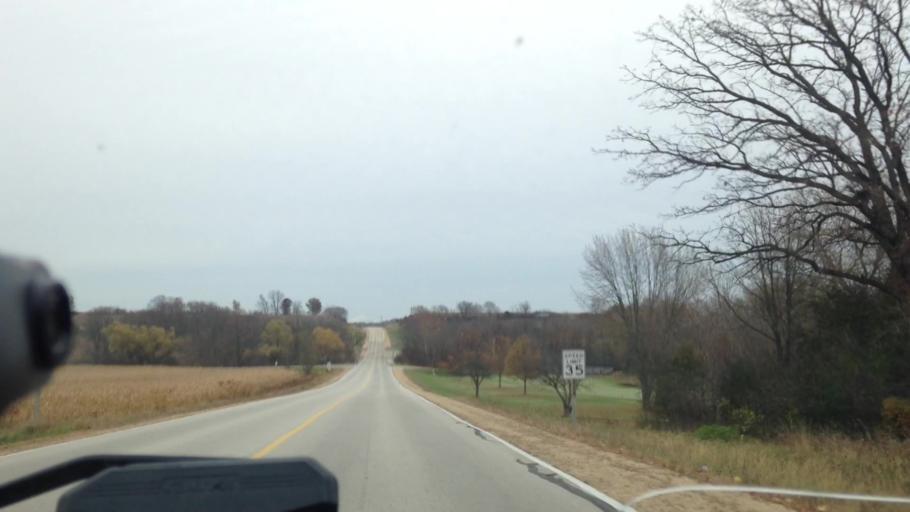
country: US
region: Wisconsin
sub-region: Dodge County
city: Mayville
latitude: 43.4938
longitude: -88.5343
